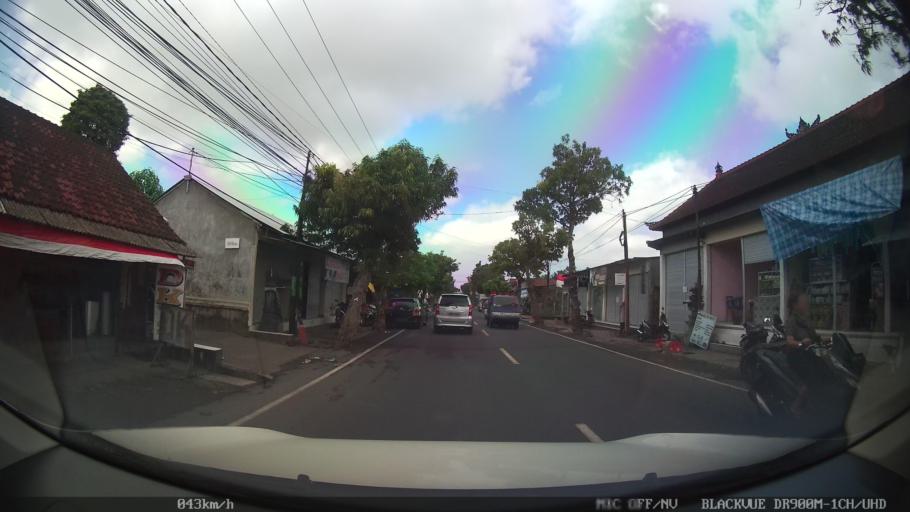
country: ID
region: Bali
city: Banjar Desa
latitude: -8.5878
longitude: 115.2825
